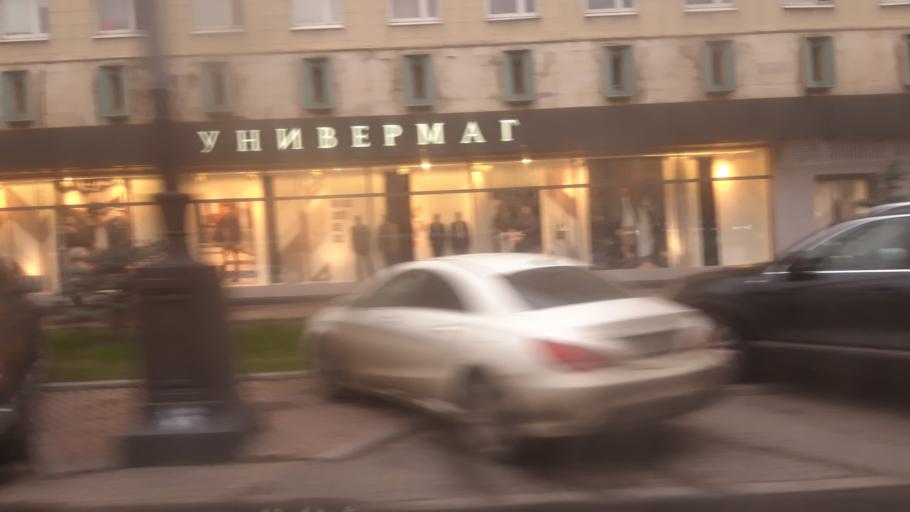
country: RU
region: St.-Petersburg
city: Kupchino
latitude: 59.8474
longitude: 30.3219
